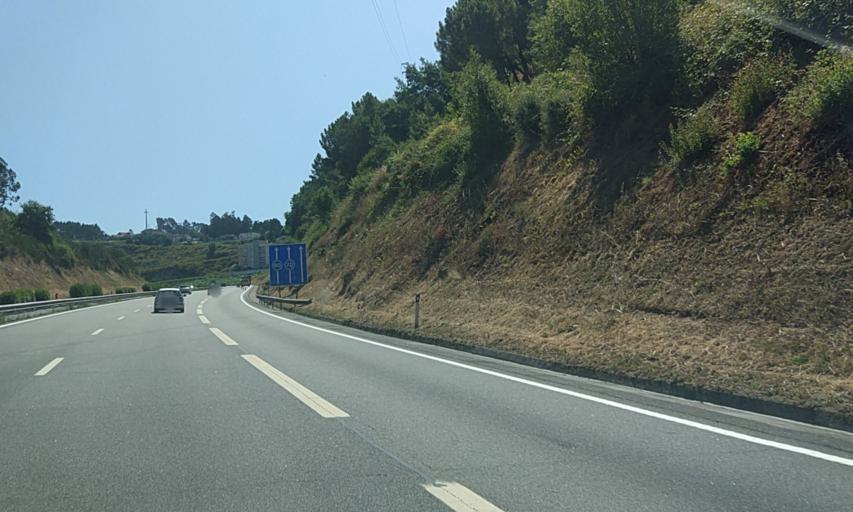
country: PT
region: Porto
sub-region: Penafiel
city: Penafiel
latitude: 41.2111
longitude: -8.2814
